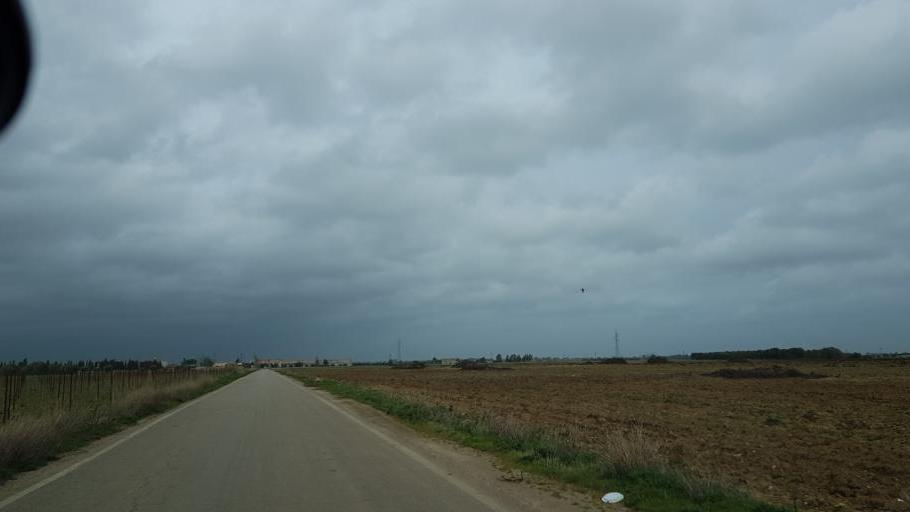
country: IT
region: Apulia
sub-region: Provincia di Brindisi
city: Brindisi
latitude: 40.6025
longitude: 17.8929
